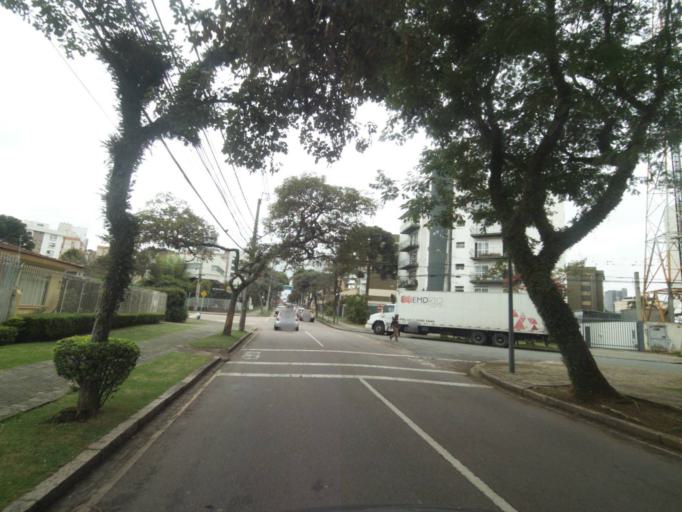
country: BR
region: Parana
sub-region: Curitiba
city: Curitiba
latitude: -25.4199
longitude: -49.2578
